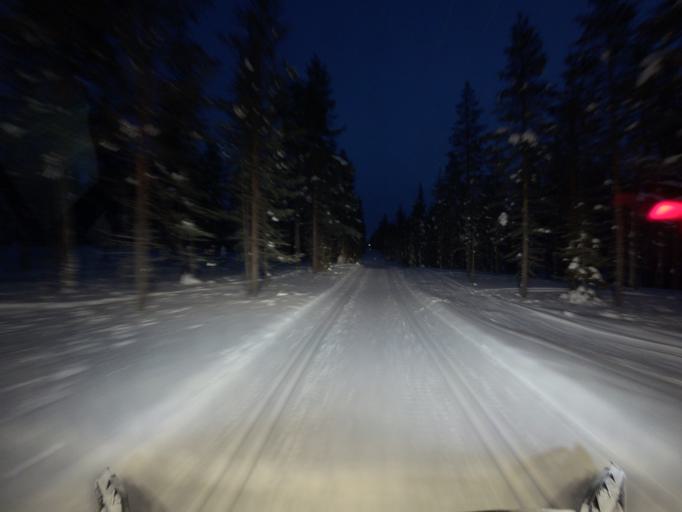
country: FI
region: Lapland
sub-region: Tunturi-Lappi
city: Kolari
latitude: 67.5945
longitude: 24.1079
